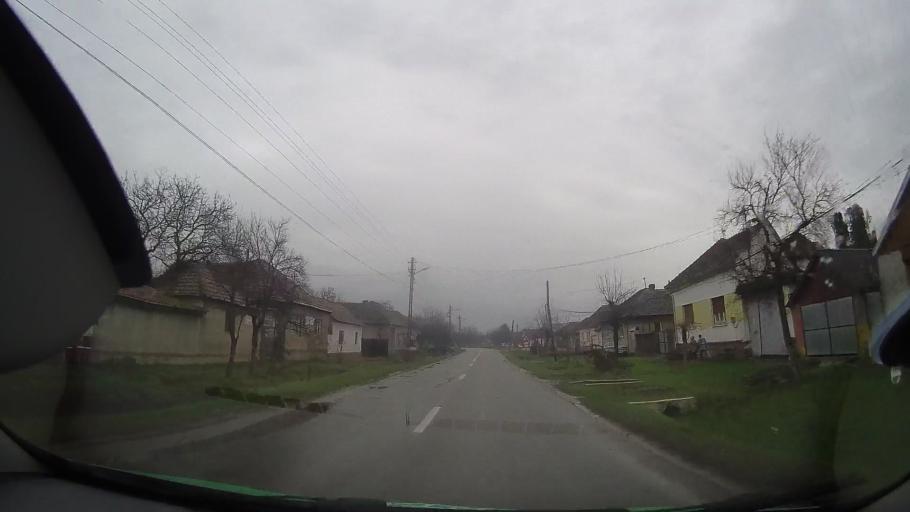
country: RO
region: Bihor
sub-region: Comuna Tinca
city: Tinca
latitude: 46.7406
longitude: 21.9490
